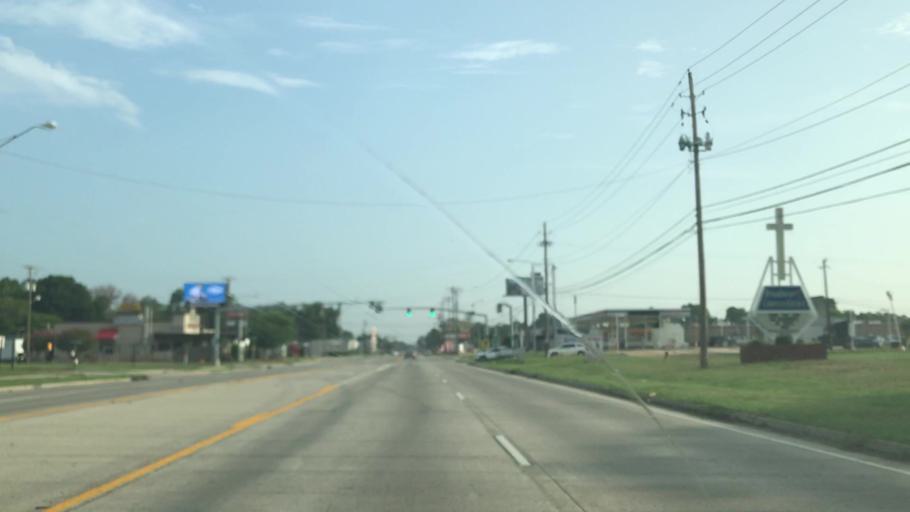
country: US
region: Louisiana
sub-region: Bossier Parish
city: Bossier City
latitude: 32.4523
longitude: -93.7221
